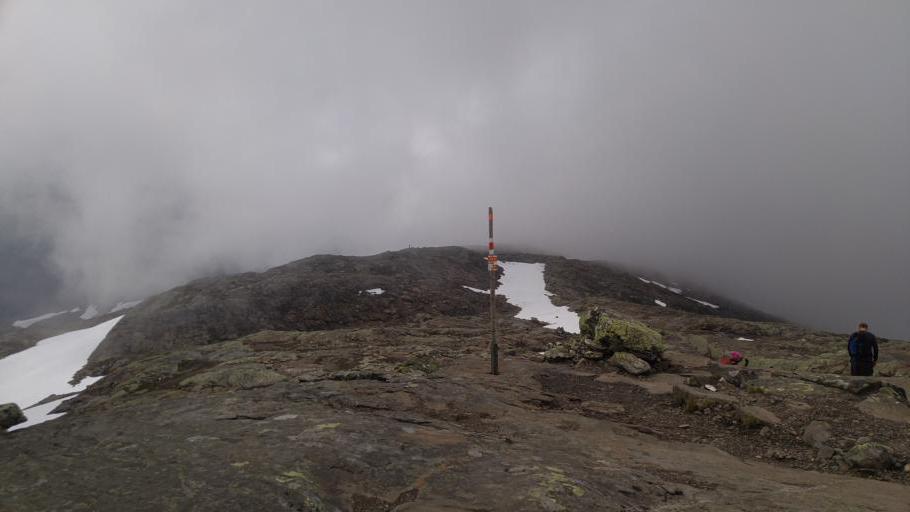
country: SE
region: Jaemtland
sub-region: Are Kommun
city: Are
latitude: 63.4308
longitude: 13.0932
